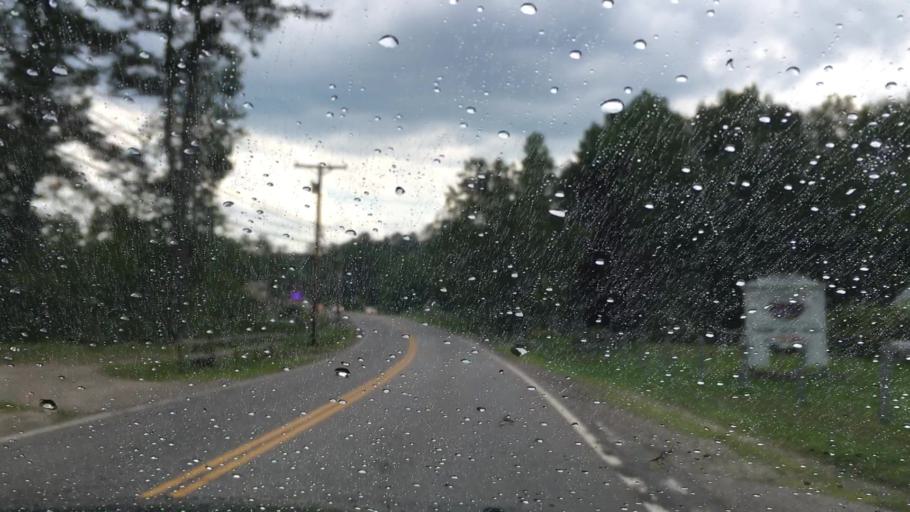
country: US
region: New Hampshire
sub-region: Belknap County
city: Meredith
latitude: 43.6843
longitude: -71.5101
